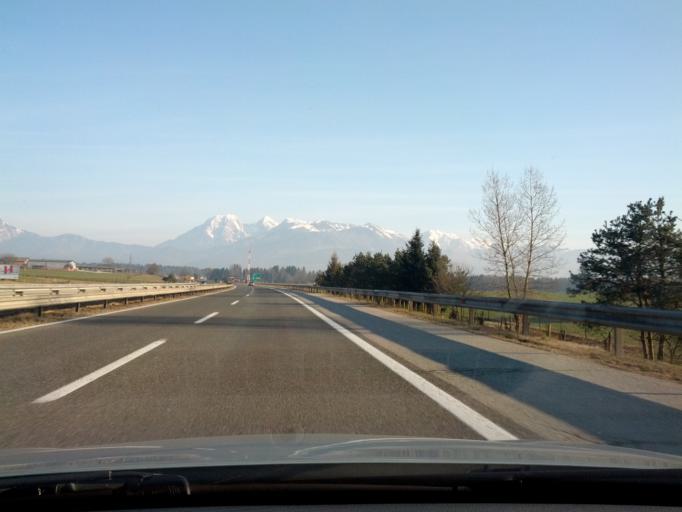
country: SI
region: Vodice
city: Vodice
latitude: 46.1680
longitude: 14.4854
